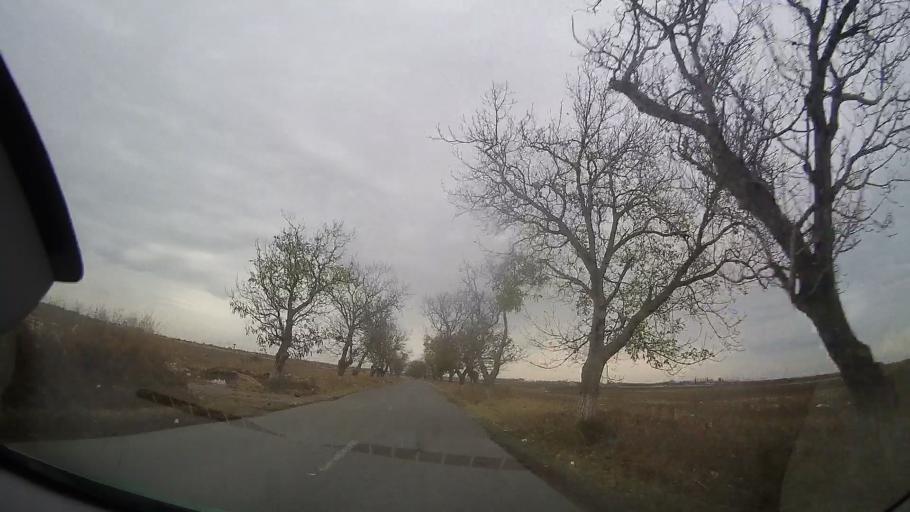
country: RO
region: Prahova
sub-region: Oras Mizil
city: Mizil
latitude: 45.0103
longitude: 26.4160
